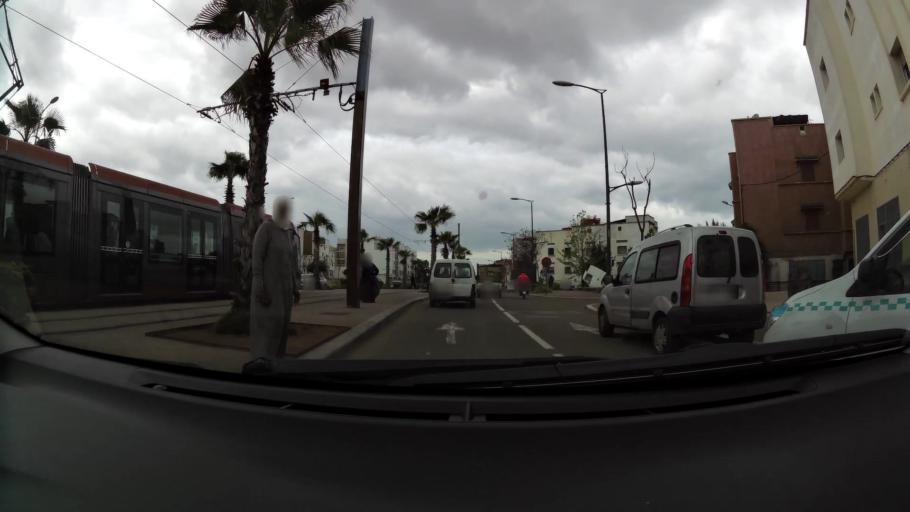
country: MA
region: Grand Casablanca
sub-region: Mediouna
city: Tit Mellil
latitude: 33.5750
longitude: -7.5401
